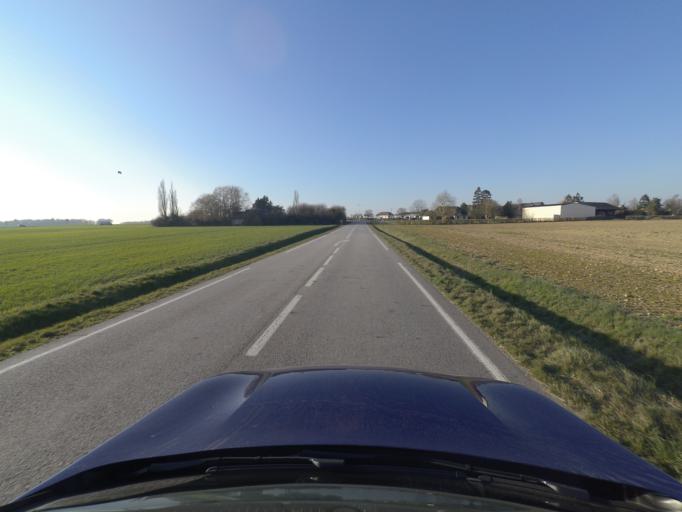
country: FR
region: Haute-Normandie
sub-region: Departement de l'Eure
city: Damville
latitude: 48.9060
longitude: 1.0247
